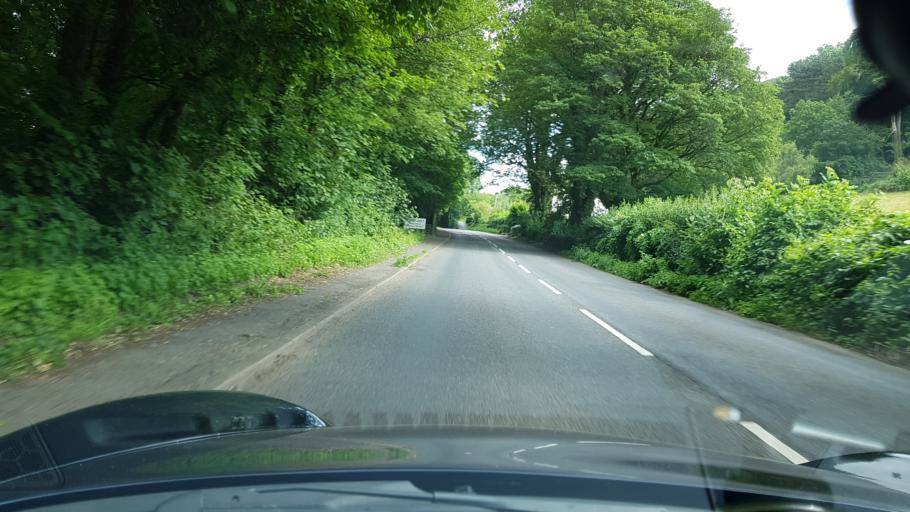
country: GB
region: Wales
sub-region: Monmouthshire
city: Abergavenny
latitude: 51.8156
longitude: -3.0409
